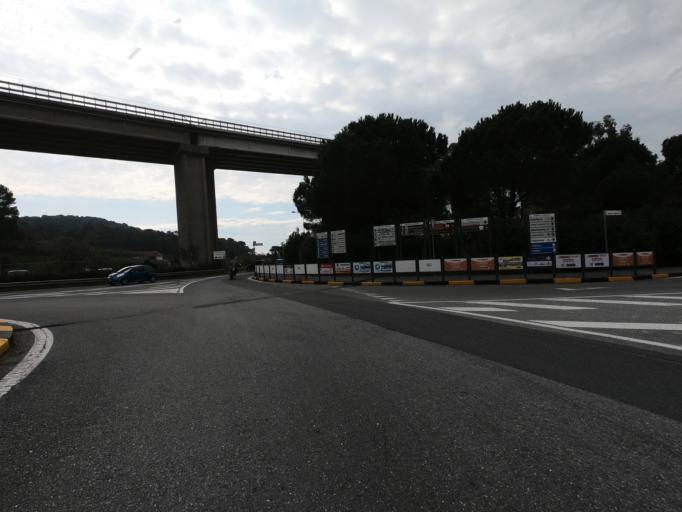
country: IT
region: Liguria
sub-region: Provincia di Savona
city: Andora
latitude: 43.9656
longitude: 8.1415
